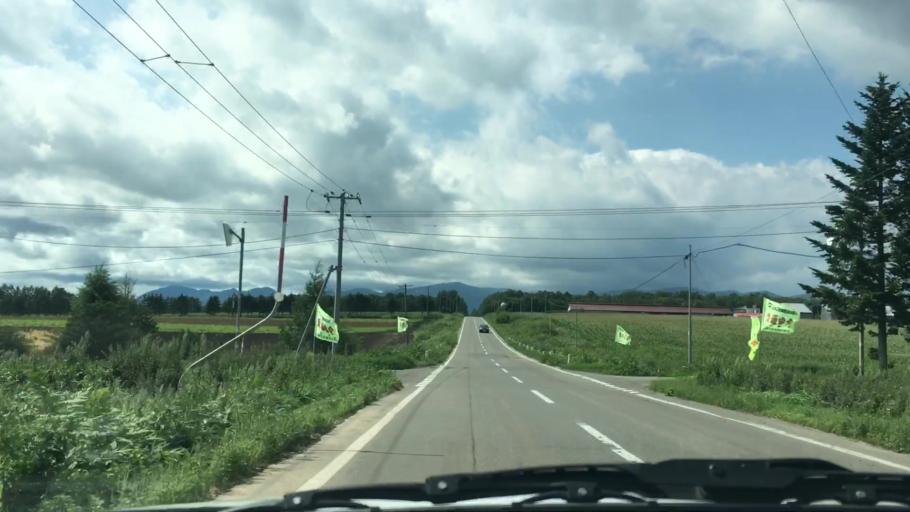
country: JP
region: Hokkaido
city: Otofuke
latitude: 43.2761
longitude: 143.3745
